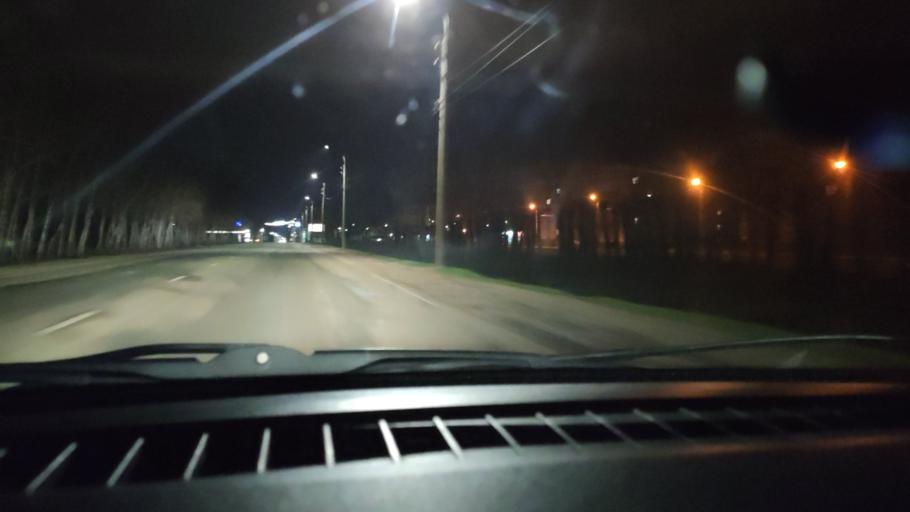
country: RU
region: Bashkortostan
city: Sterlitamak
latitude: 53.6405
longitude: 55.9018
